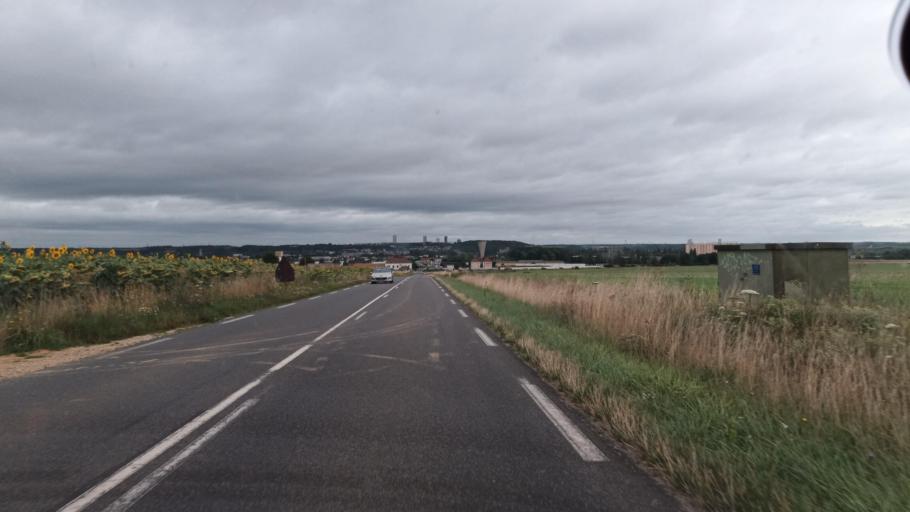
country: FR
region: Ile-de-France
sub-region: Departement de Seine-et-Marne
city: Montereau-Fault-Yonne
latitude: 48.3557
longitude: 2.9572
